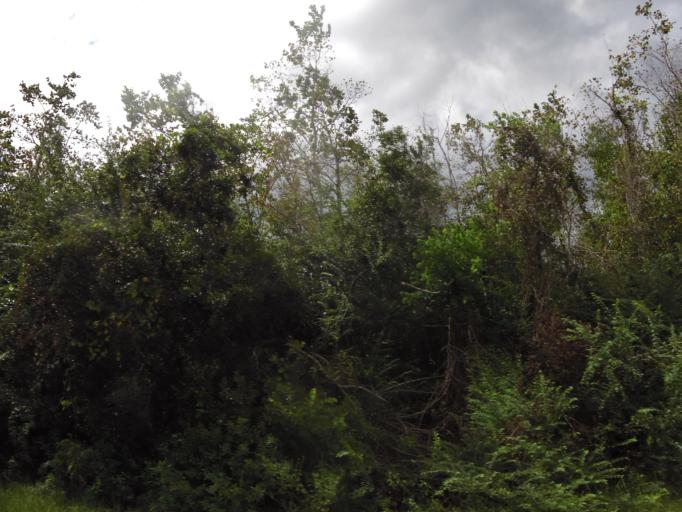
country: US
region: Georgia
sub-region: Brantley County
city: Nahunta
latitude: 31.2022
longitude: -81.9851
